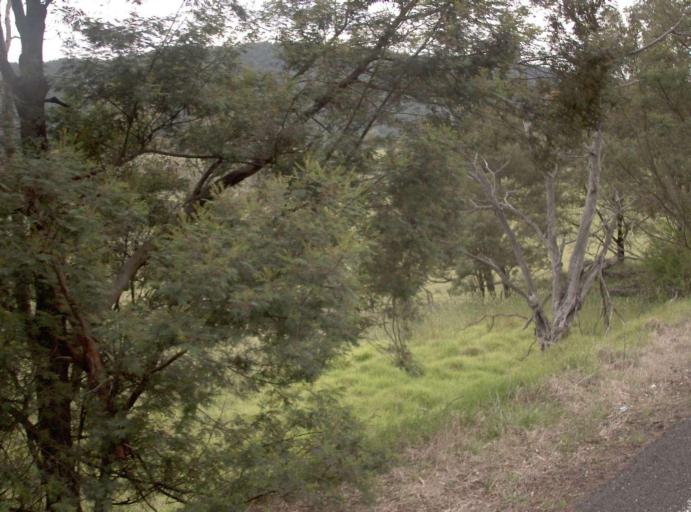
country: AU
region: Victoria
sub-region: East Gippsland
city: Bairnsdale
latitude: -37.5622
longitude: 147.1923
